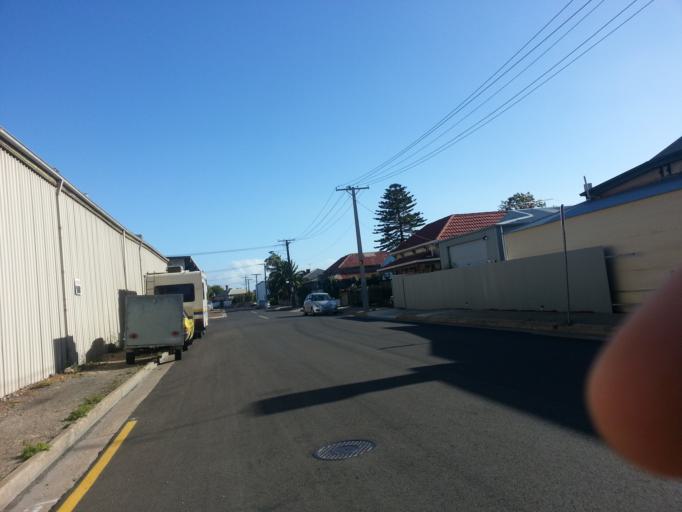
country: AU
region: South Australia
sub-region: Port Adelaide Enfield
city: Alberton
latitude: -34.8456
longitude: 138.5126
